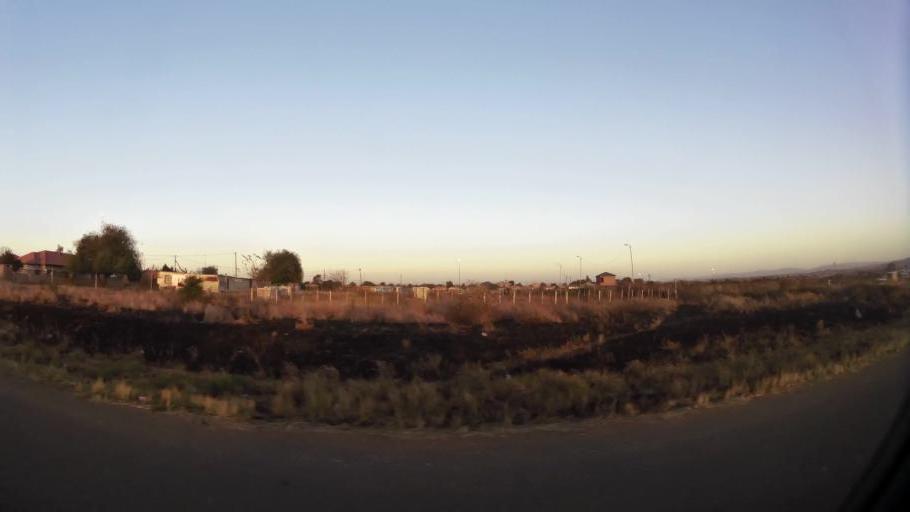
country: ZA
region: North-West
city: Ga-Rankuwa
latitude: -25.5709
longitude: 28.0529
